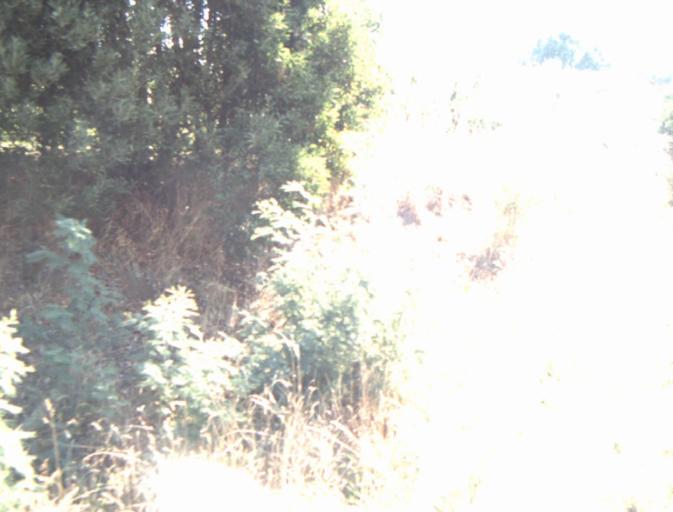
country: AU
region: Tasmania
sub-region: Launceston
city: Mayfield
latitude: -41.3460
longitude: 147.0949
